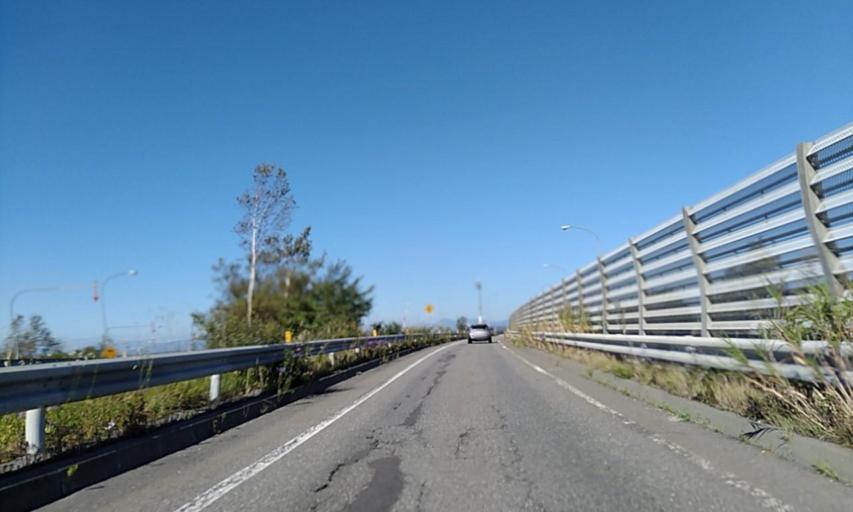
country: JP
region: Hokkaido
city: Tomakomai
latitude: 42.6766
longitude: 141.7141
